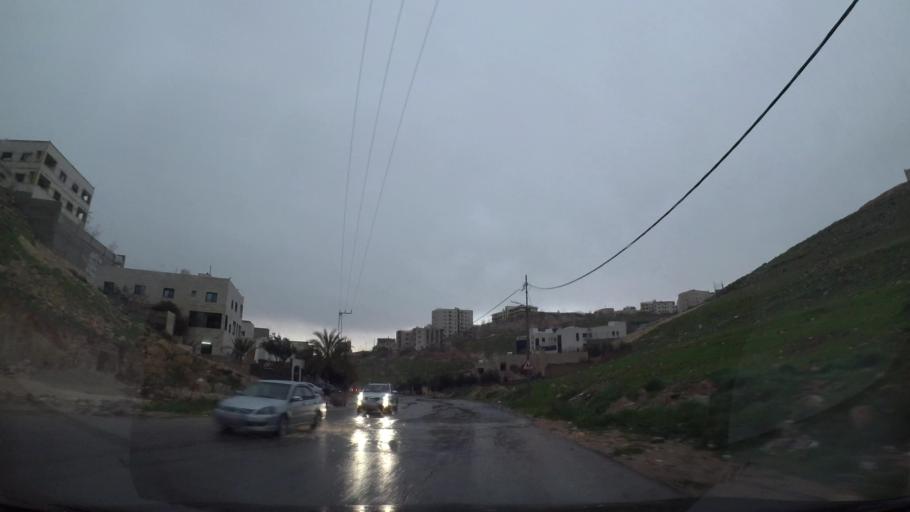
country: JO
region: Amman
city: Amman
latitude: 31.9945
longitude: 35.9705
